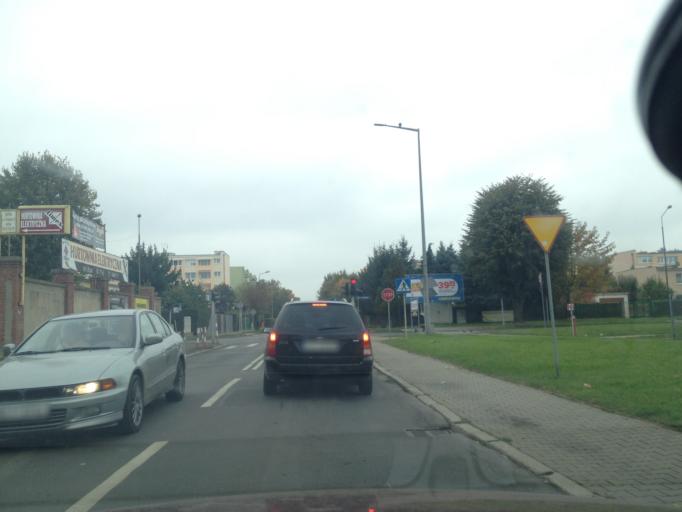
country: PL
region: Lower Silesian Voivodeship
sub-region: Powiat zgorzelecki
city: Zgorzelec
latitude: 51.1520
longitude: 15.0147
